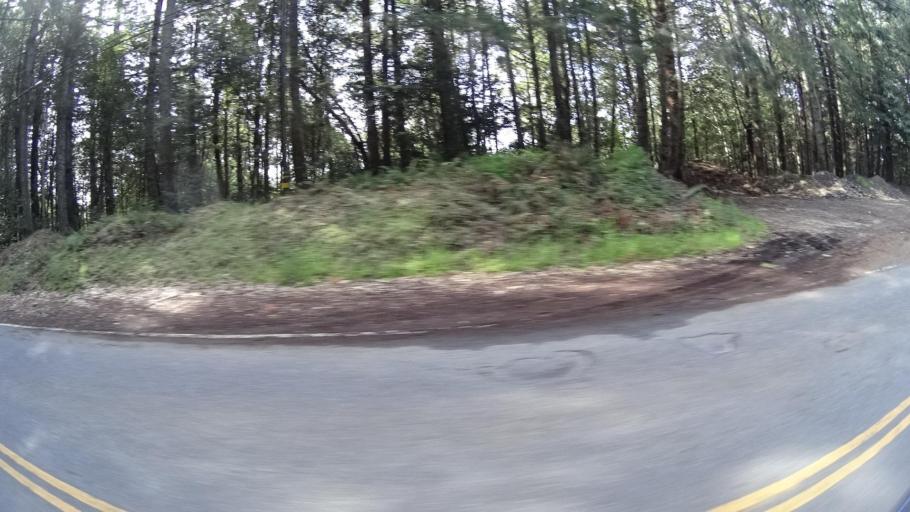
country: US
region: California
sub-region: Humboldt County
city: Bayside
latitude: 40.7483
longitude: -123.9739
